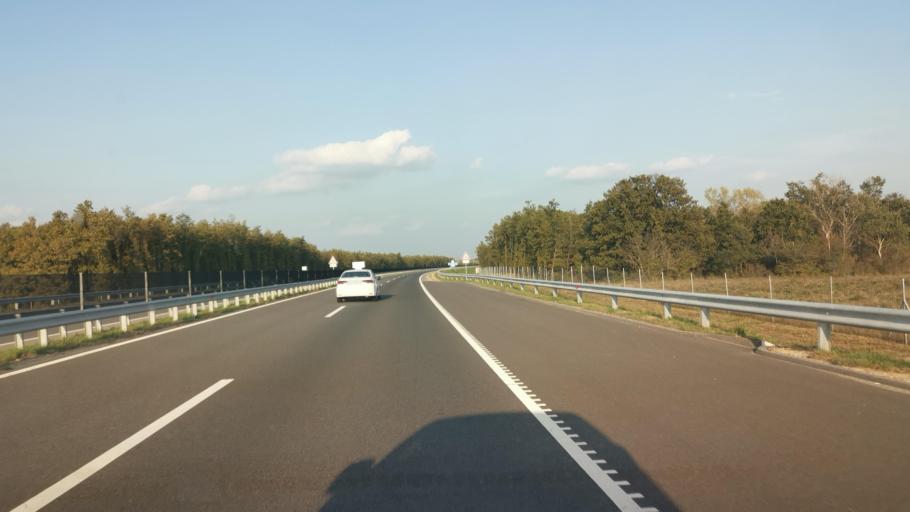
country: HU
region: Gyor-Moson-Sopron
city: Fertoszentmiklos
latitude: 47.5818
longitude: 16.9233
